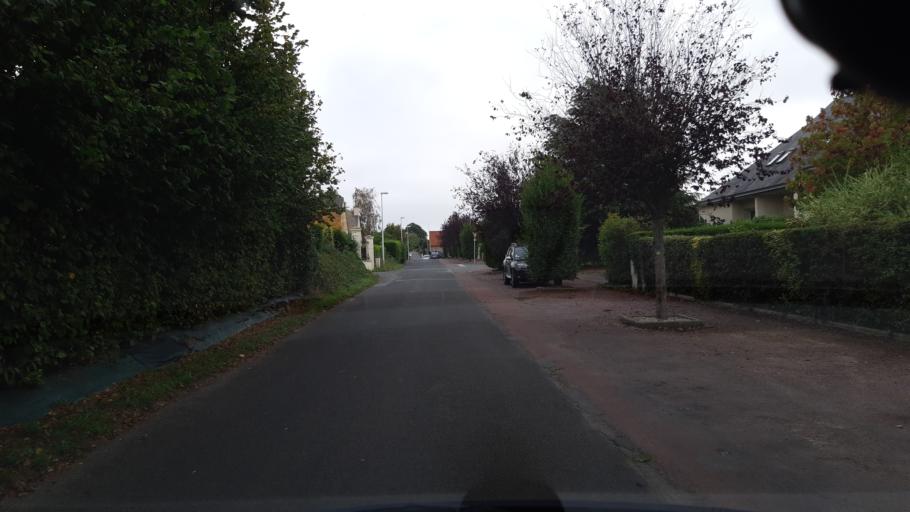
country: FR
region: Lower Normandy
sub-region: Departement de la Manche
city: Donville-les-Bains
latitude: 48.8407
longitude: -1.5553
